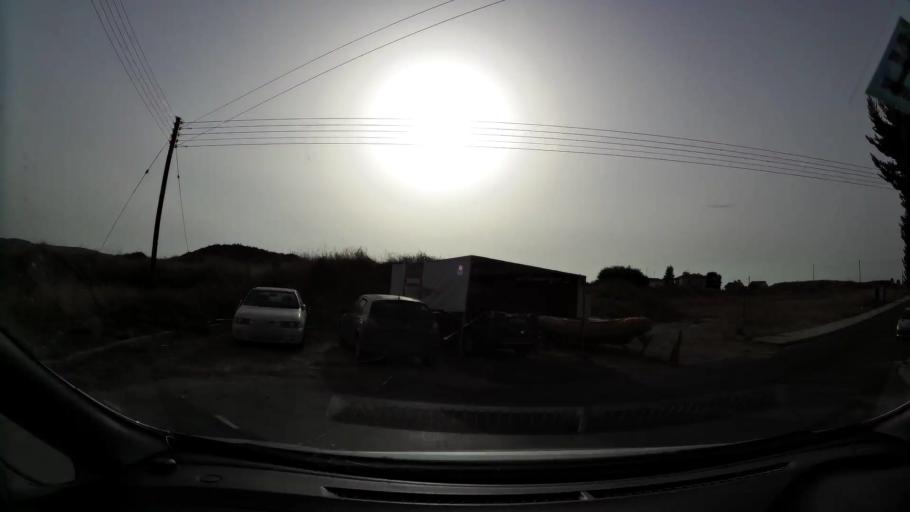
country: CY
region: Lefkosia
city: Geri
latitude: 35.0644
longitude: 33.3919
